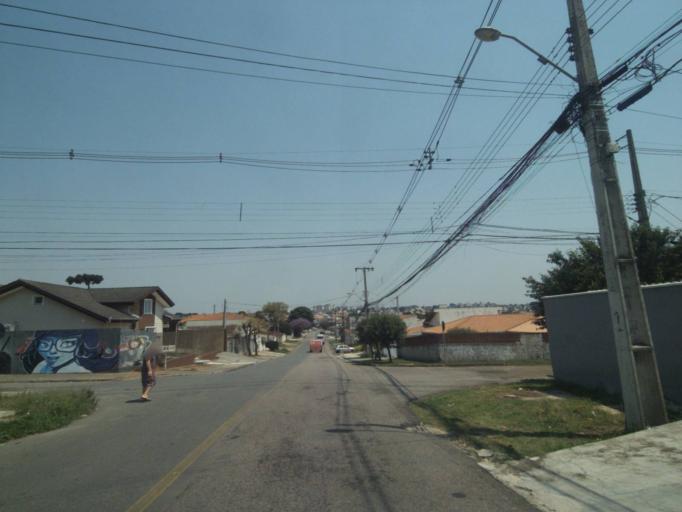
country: BR
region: Parana
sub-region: Sao Jose Dos Pinhais
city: Sao Jose dos Pinhais
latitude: -25.5113
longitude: -49.2692
